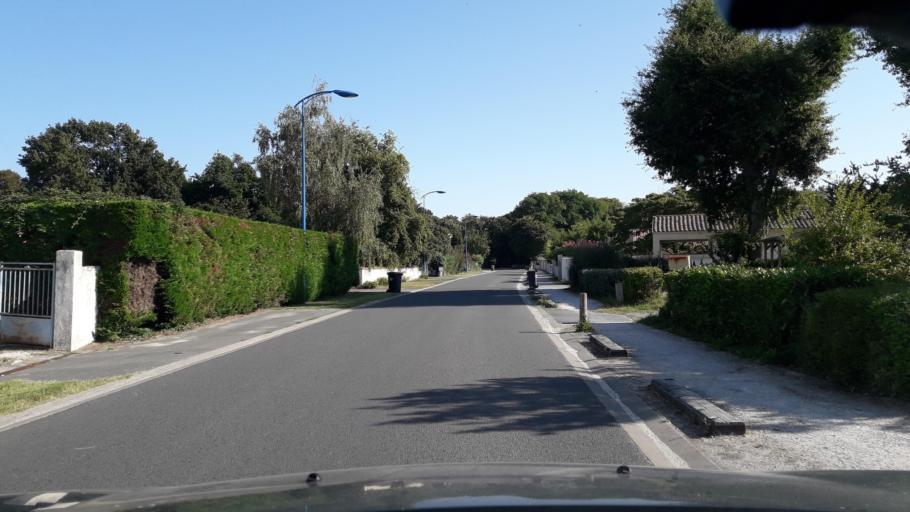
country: FR
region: Poitou-Charentes
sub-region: Departement de la Charente-Maritime
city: Etaules
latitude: 45.7272
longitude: -1.1003
